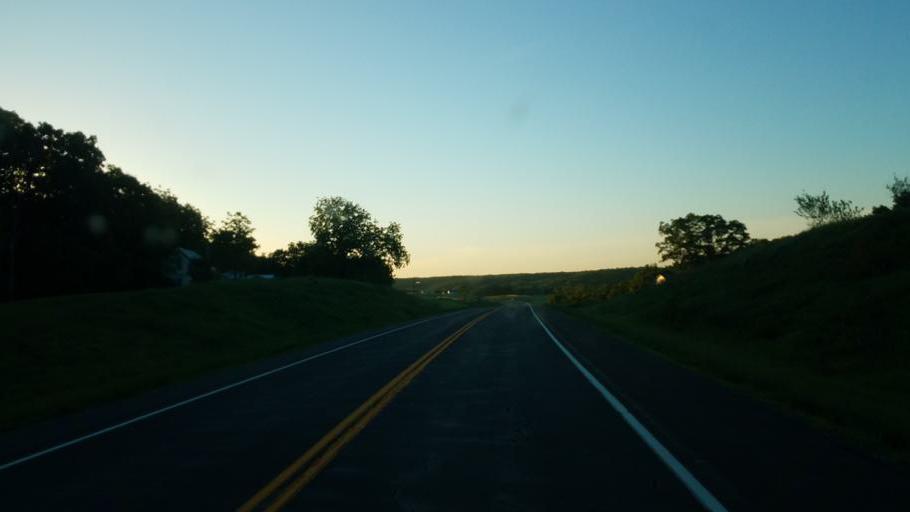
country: US
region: Missouri
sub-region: Schuyler County
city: Lancaster
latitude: 40.4882
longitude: -92.6428
